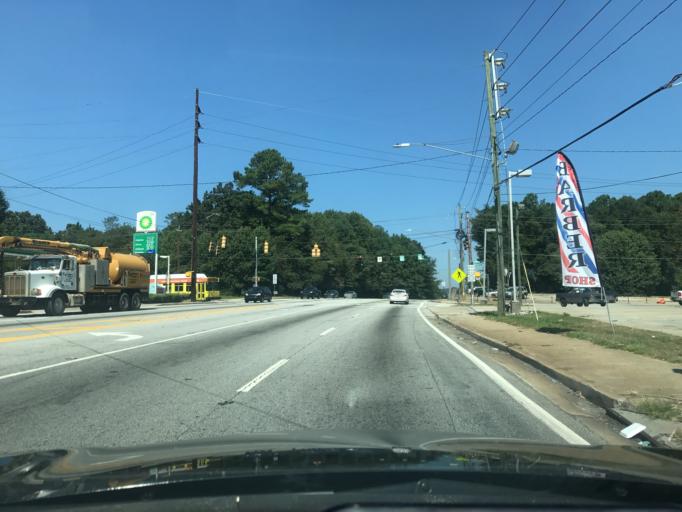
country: US
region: Georgia
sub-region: Cobb County
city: Vinings
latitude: 33.7875
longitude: -84.4939
